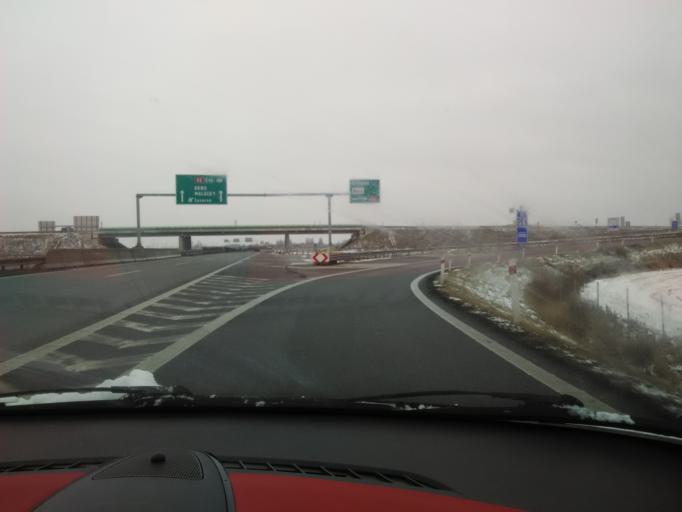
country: SK
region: Bratislavsky
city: Stupava
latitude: 48.2473
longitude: 17.0136
